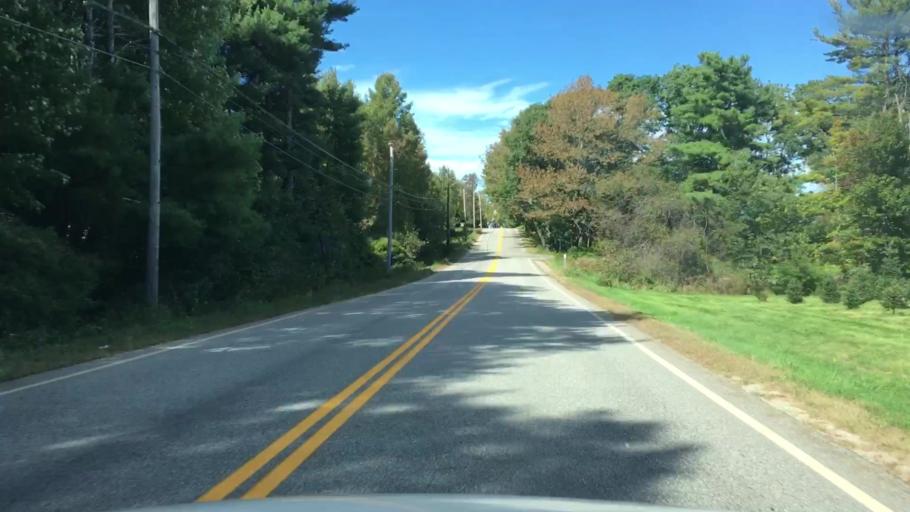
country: US
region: Maine
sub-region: Cumberland County
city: West Scarborough
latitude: 43.6174
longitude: -70.4062
